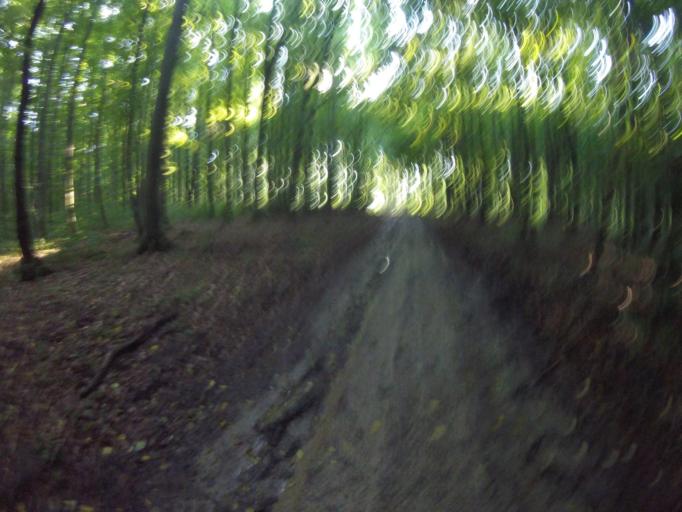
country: HU
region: Zala
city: Letenye
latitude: 46.5030
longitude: 16.7280
